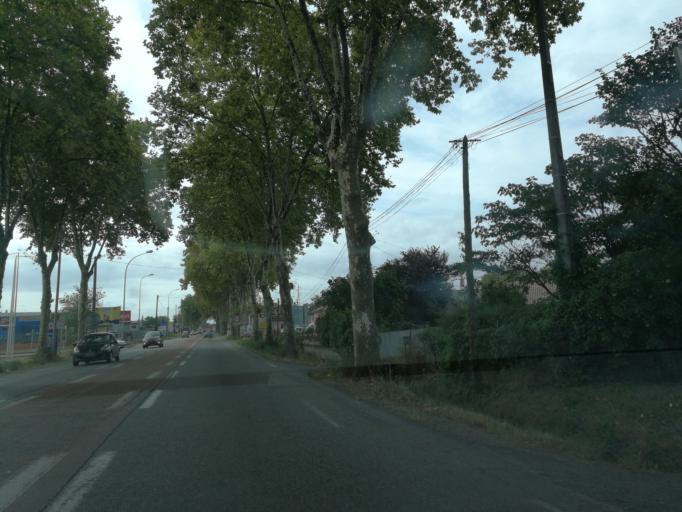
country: FR
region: Midi-Pyrenees
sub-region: Departement de la Haute-Garonne
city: Aucamville
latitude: 43.6719
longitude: 1.4101
